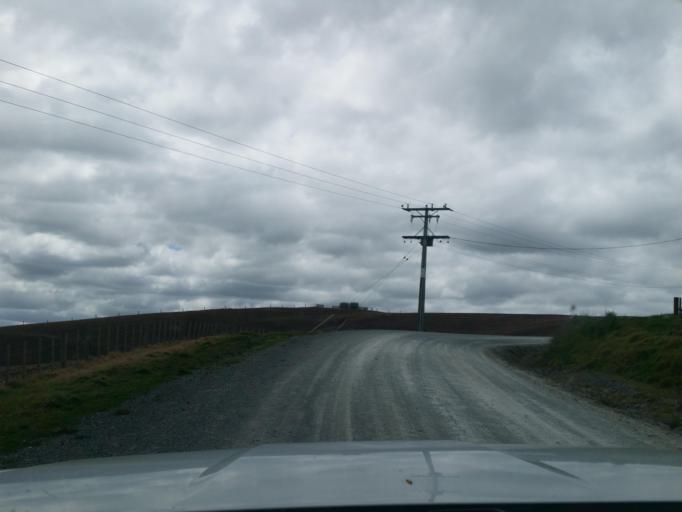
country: NZ
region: Auckland
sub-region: Auckland
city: Wellsford
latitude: -36.2868
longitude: 174.3463
